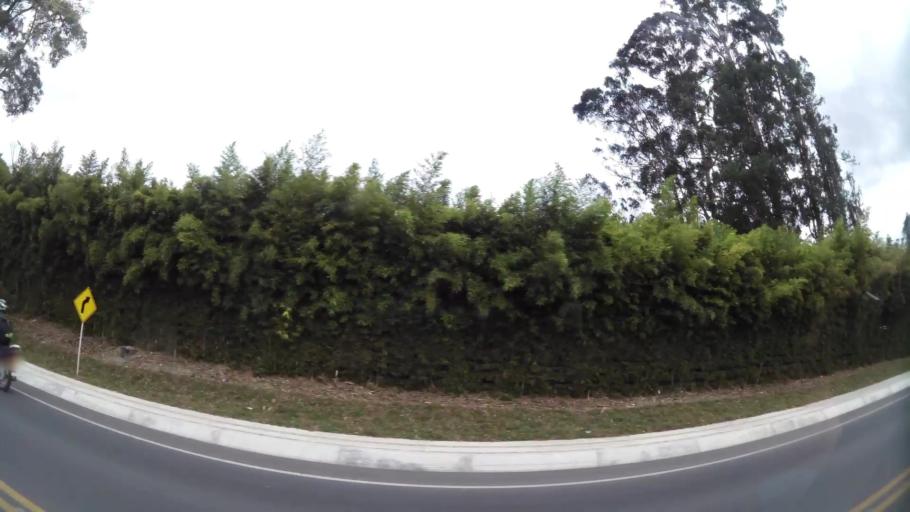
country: CO
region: Antioquia
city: Rionegro
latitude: 6.1442
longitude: -75.4312
